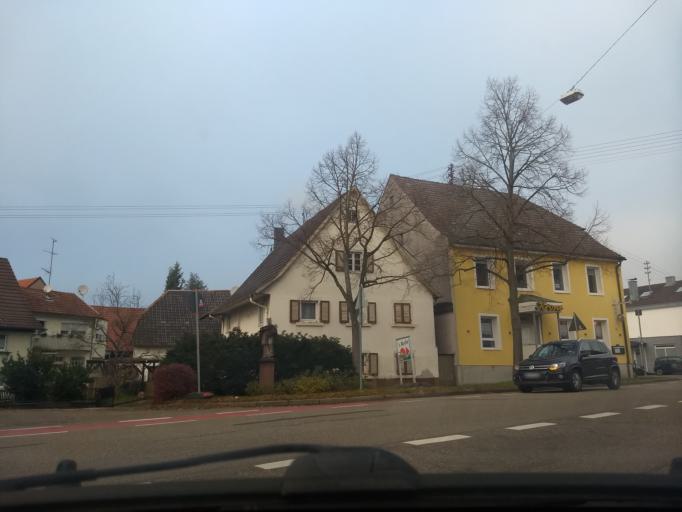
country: DE
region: Baden-Wuerttemberg
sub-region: Karlsruhe Region
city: Kuppenheim
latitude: 48.8064
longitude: 8.2222
